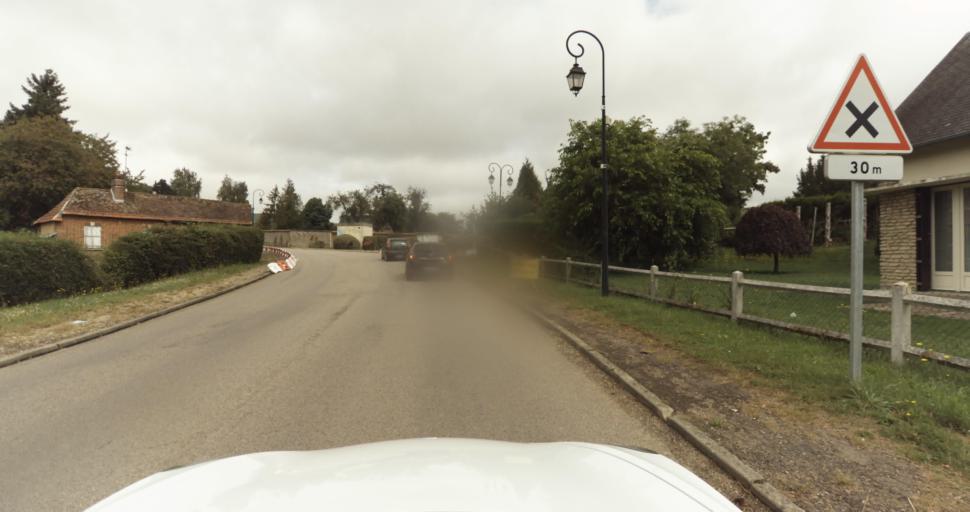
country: FR
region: Haute-Normandie
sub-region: Departement de l'Eure
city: Aviron
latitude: 49.0453
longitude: 1.0879
